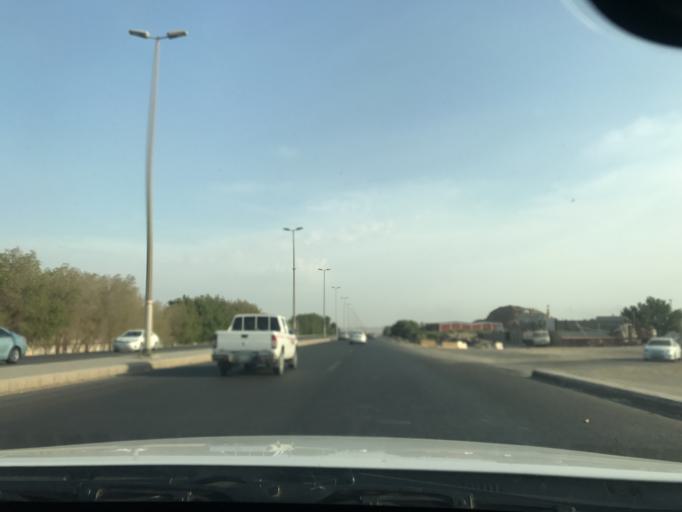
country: SA
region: Makkah
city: Jeddah
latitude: 21.4024
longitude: 39.4268
